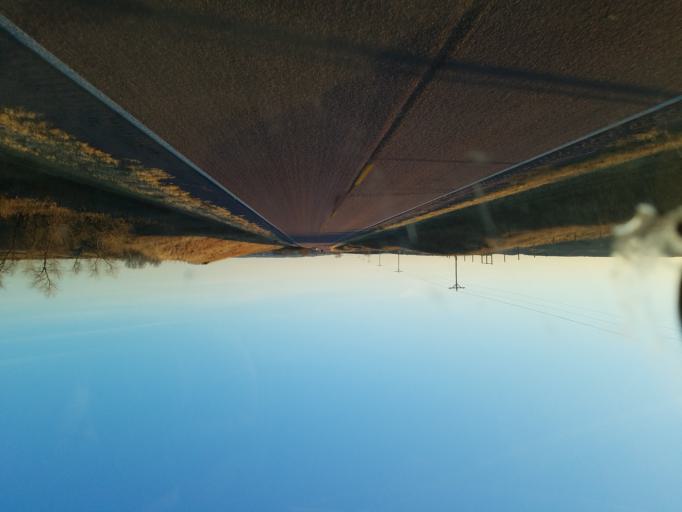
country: US
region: South Dakota
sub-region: Bon Homme County
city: Springfield
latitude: 42.7377
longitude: -97.9072
